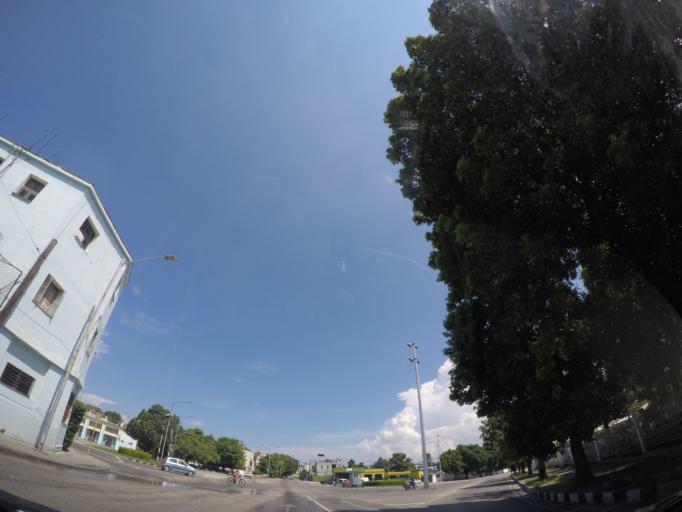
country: CU
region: La Habana
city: Havana
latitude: 23.1287
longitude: -82.3926
